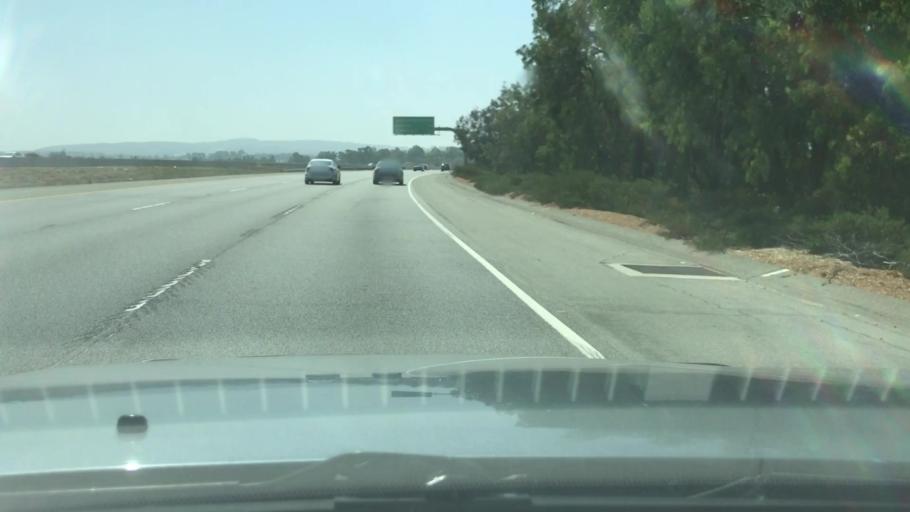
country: US
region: California
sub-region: Orange County
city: Irvine
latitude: 33.6537
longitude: -117.8635
